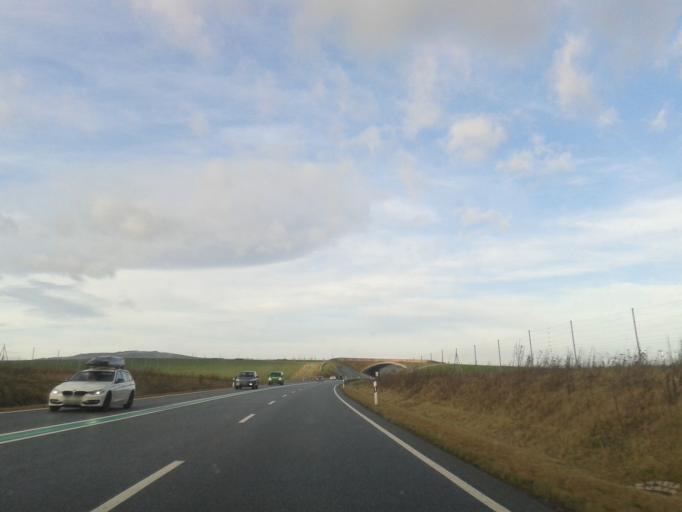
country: DE
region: Saxony
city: Herrnhut
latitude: 50.9746
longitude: 14.7340
